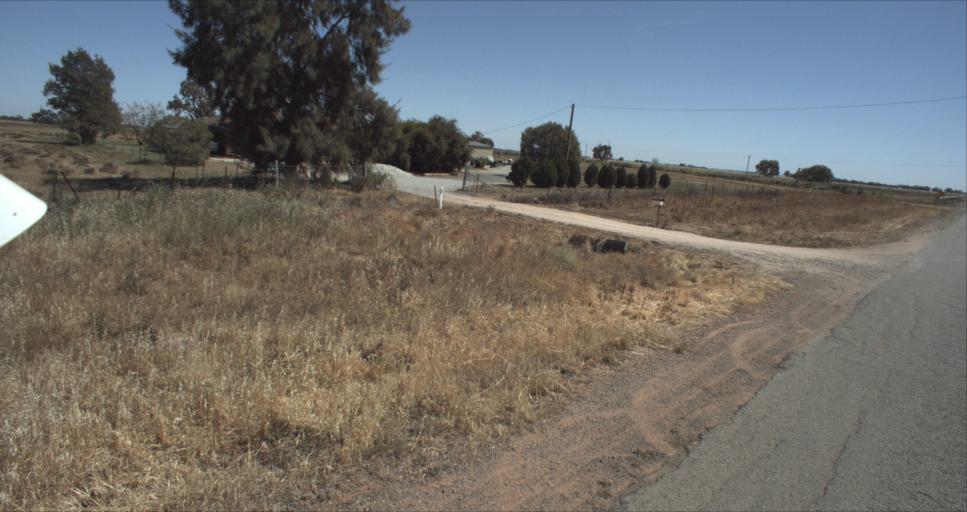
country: AU
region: New South Wales
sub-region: Leeton
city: Leeton
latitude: -34.5691
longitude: 146.3110
